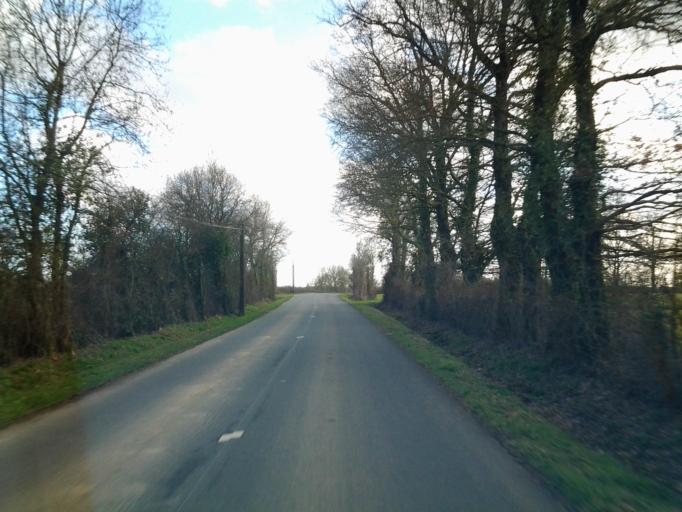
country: FR
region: Pays de la Loire
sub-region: Departement de la Vendee
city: Chateau-Guibert
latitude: 46.6188
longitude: -1.2352
